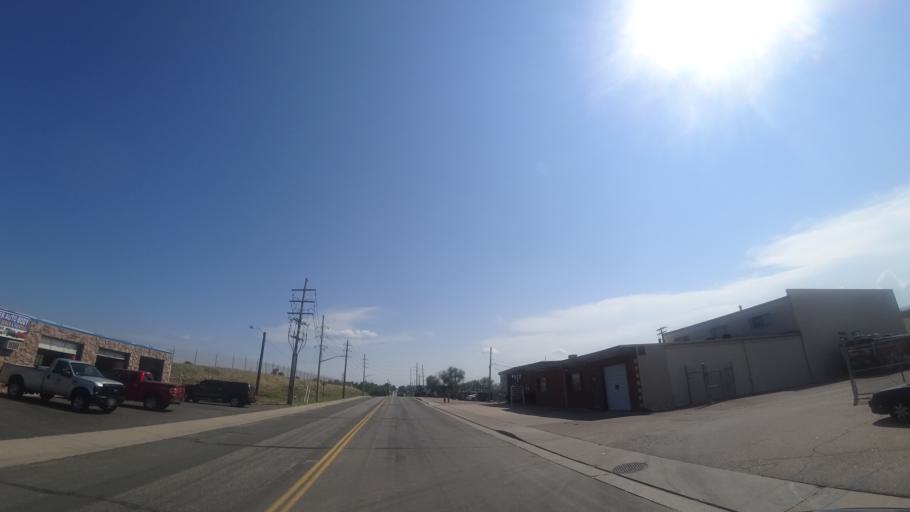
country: US
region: Colorado
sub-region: Arapahoe County
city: Littleton
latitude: 39.6323
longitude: -105.0066
